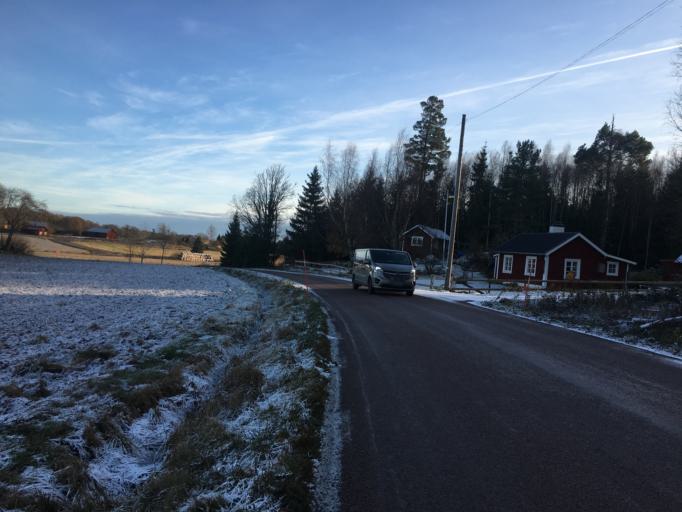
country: SE
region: Vaestmanland
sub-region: Vasteras
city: Vasteras
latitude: 59.6428
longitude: 16.4742
